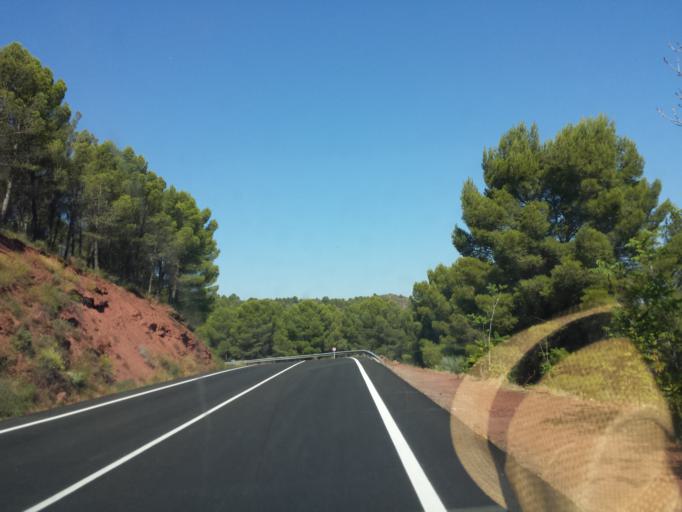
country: ES
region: Aragon
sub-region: Provincia de Zaragoza
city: Nuevalos
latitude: 41.2124
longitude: -1.7614
